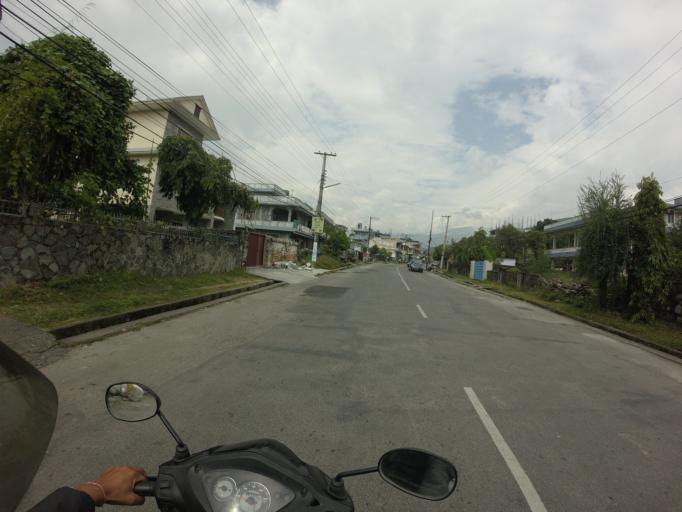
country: NP
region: Western Region
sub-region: Gandaki Zone
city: Pokhara
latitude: 28.2179
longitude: 83.9976
